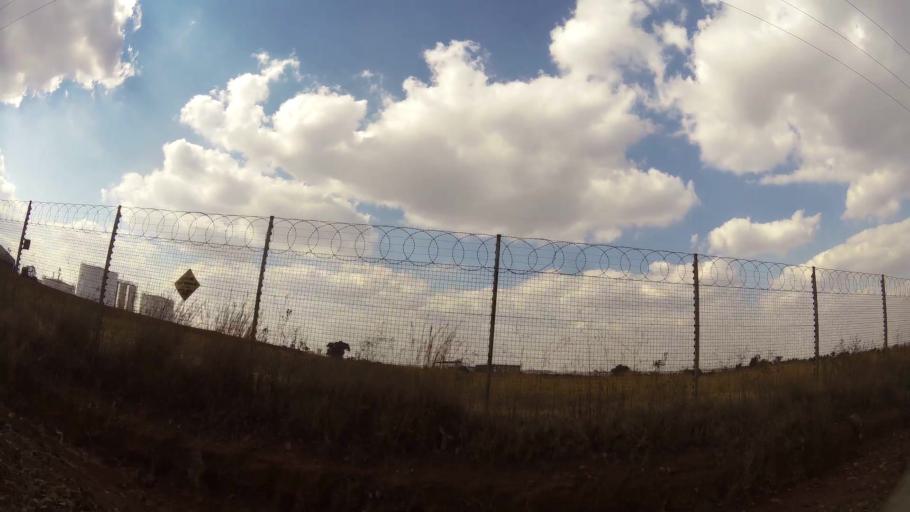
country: ZA
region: Mpumalanga
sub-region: Nkangala District Municipality
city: Delmas
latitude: -26.1306
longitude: 28.6776
